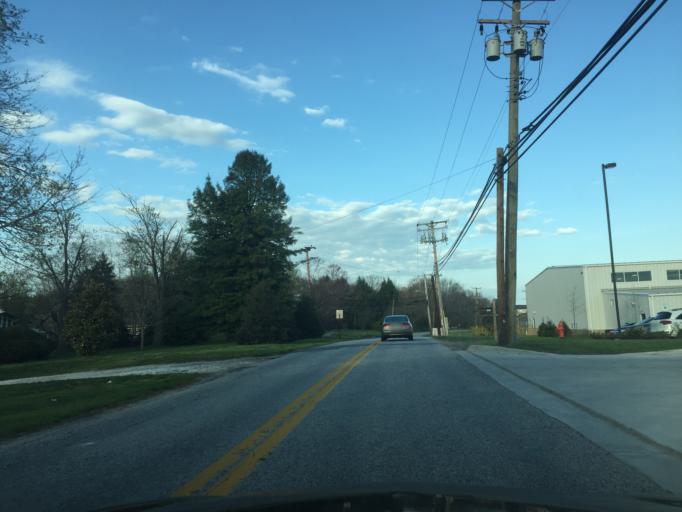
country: US
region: Maryland
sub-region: Baltimore County
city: Perry Hall
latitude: 39.4023
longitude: -76.4497
